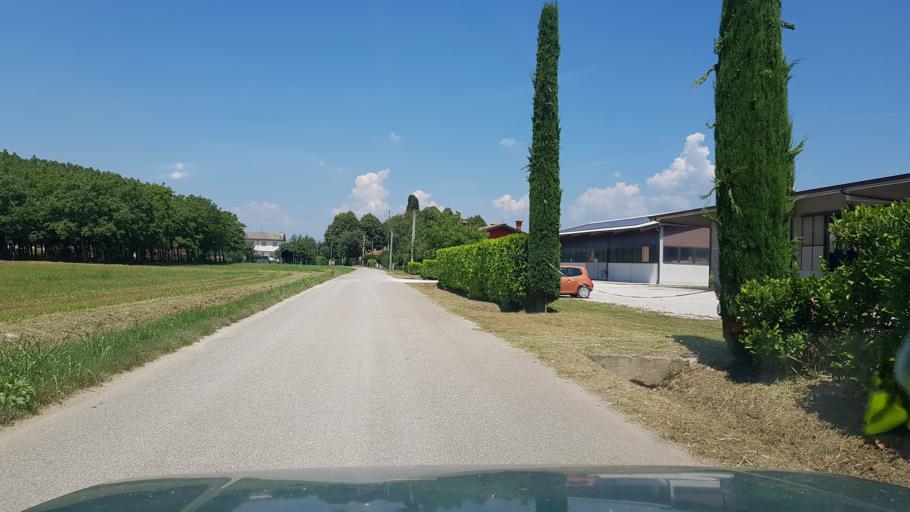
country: IT
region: Friuli Venezia Giulia
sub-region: Provincia di Gorizia
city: Farra d'Isonzo
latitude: 45.9115
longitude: 13.5366
